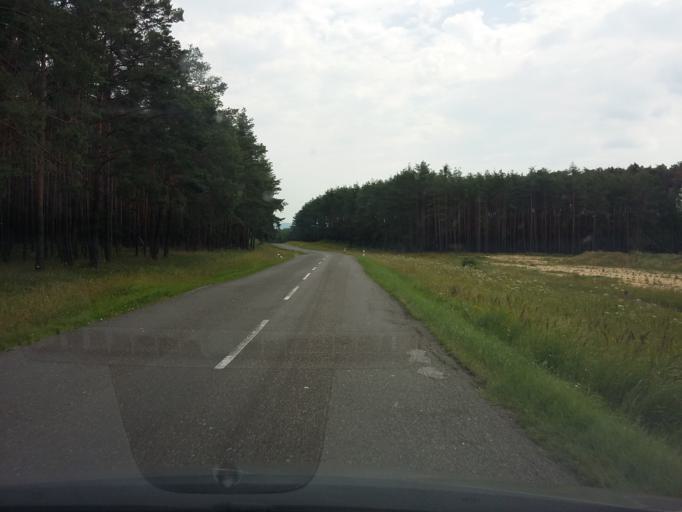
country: SK
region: Bratislavsky
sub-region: Okres Malacky
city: Malacky
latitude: 48.4586
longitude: 17.1310
